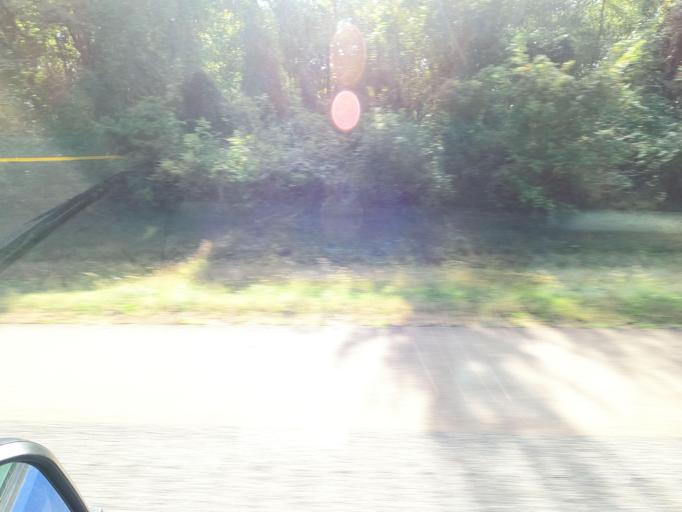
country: US
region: Tennessee
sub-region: Haywood County
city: Brownsville
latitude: 35.5552
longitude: -89.1942
